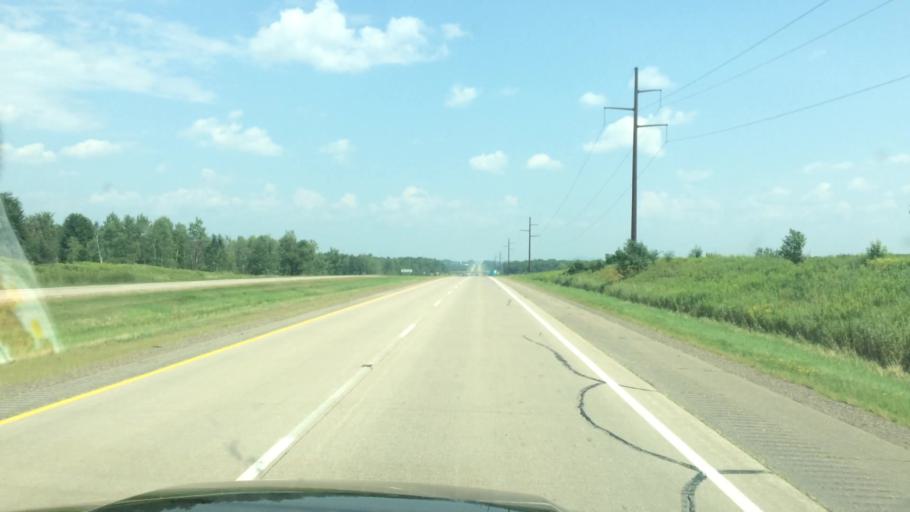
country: US
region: Wisconsin
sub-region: Marathon County
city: Edgar
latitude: 44.9442
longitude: -89.9892
